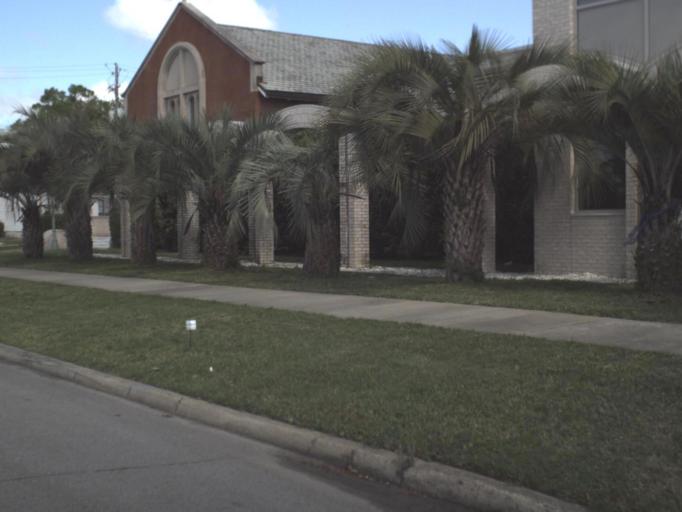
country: US
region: Florida
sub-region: Escambia County
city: Pensacola
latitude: 30.4113
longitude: -87.2277
